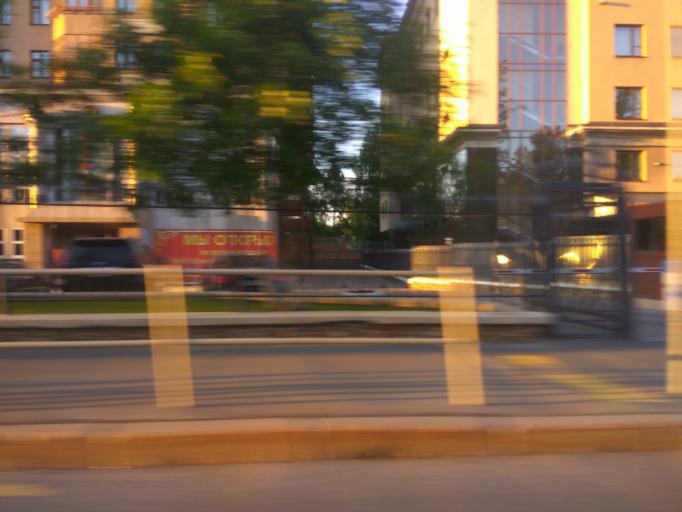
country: RU
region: Moscow
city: Vorob'yovo
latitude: 55.7136
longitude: 37.5246
